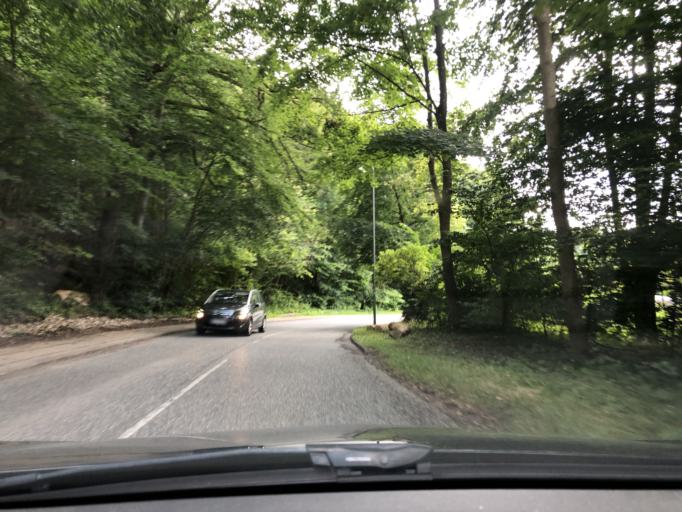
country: DK
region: South Denmark
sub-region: Vejle Kommune
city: Vejle
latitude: 55.7577
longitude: 9.5329
